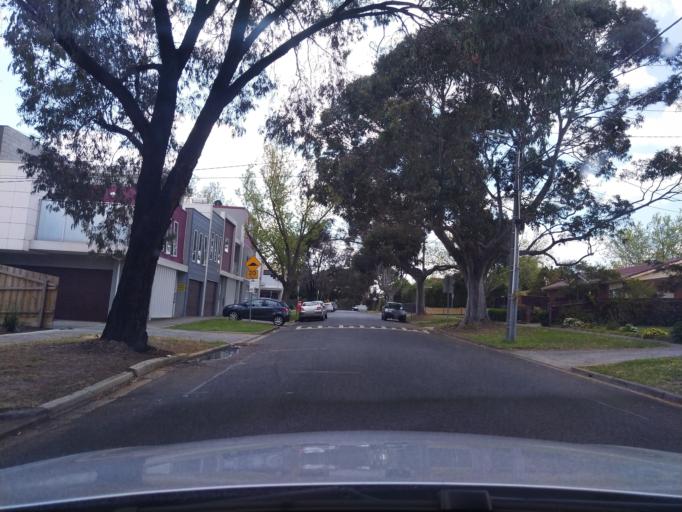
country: AU
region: Victoria
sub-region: Banyule
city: Heidelberg Heights
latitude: -37.7504
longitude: 145.0551
